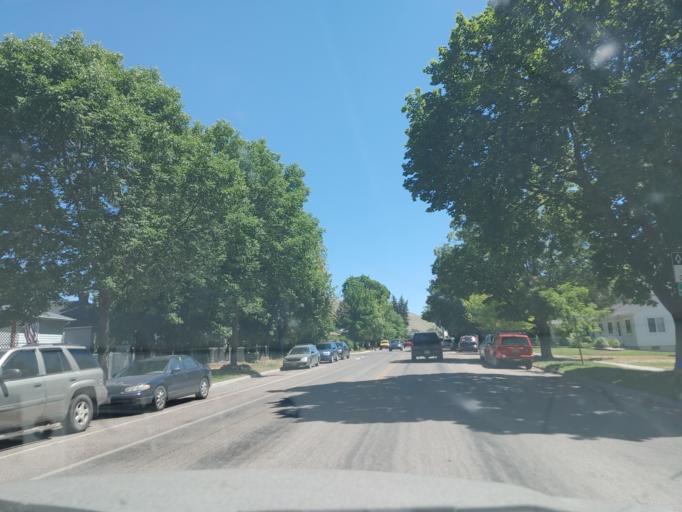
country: US
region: Montana
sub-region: Missoula County
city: Missoula
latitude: 46.8670
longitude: -114.0143
